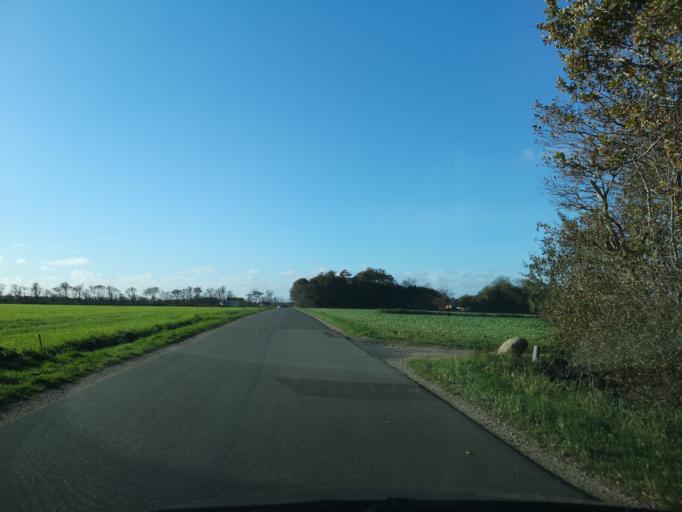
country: DK
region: Central Jutland
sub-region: Ringkobing-Skjern Kommune
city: Tarm
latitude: 55.8048
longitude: 8.4795
